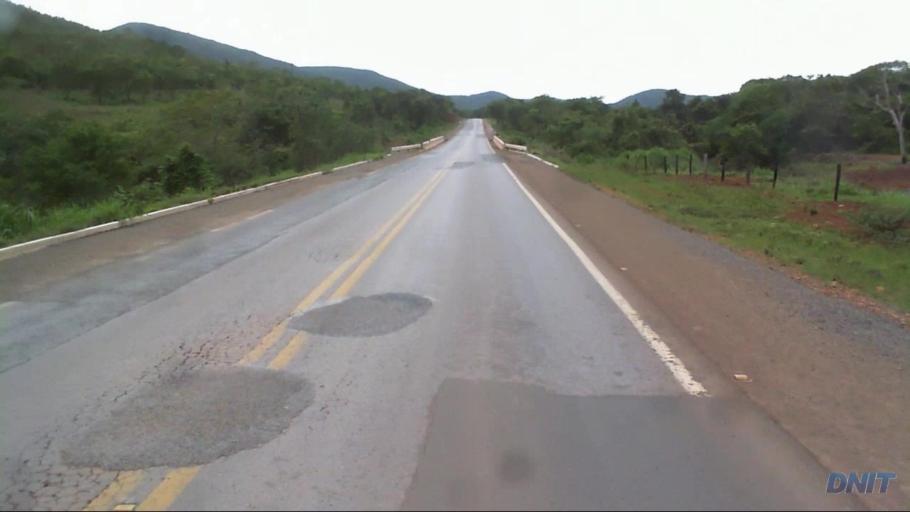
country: BR
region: Goias
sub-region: Barro Alto
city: Barro Alto
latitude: -14.8888
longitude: -48.9778
